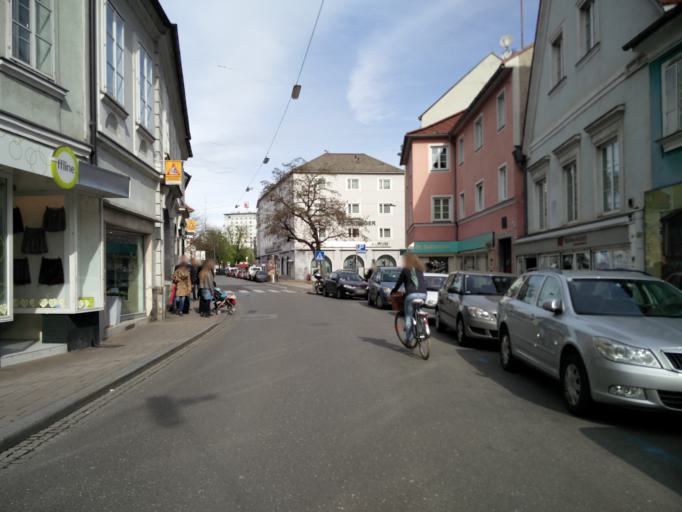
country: AT
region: Styria
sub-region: Graz Stadt
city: Graz
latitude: 47.0735
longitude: 15.4330
